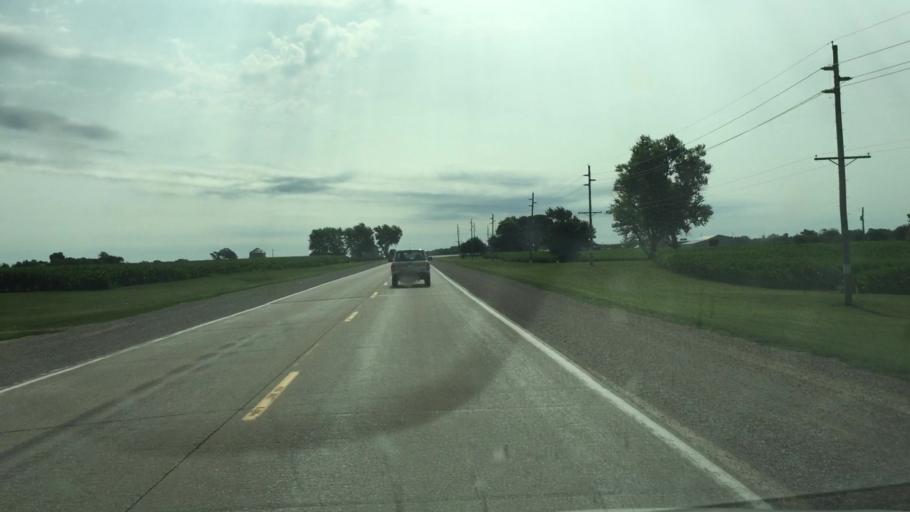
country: US
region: Illinois
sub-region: Hancock County
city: Nauvoo
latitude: 40.6390
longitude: -91.5303
